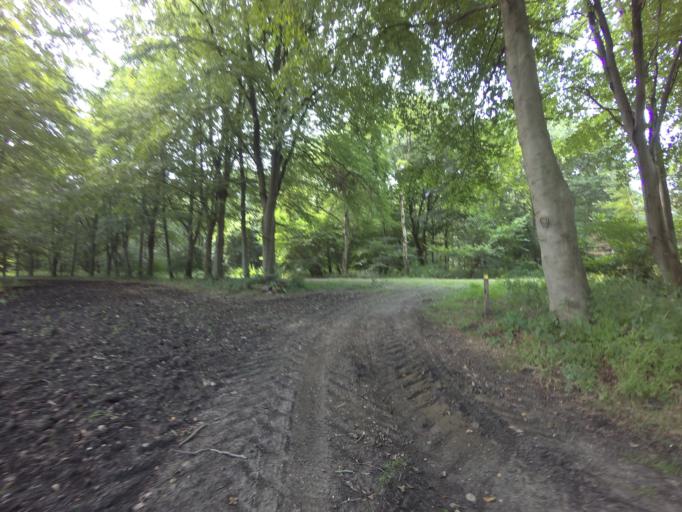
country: NL
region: North Holland
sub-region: Gemeente Huizen
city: Huizen
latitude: 52.3277
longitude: 5.2849
